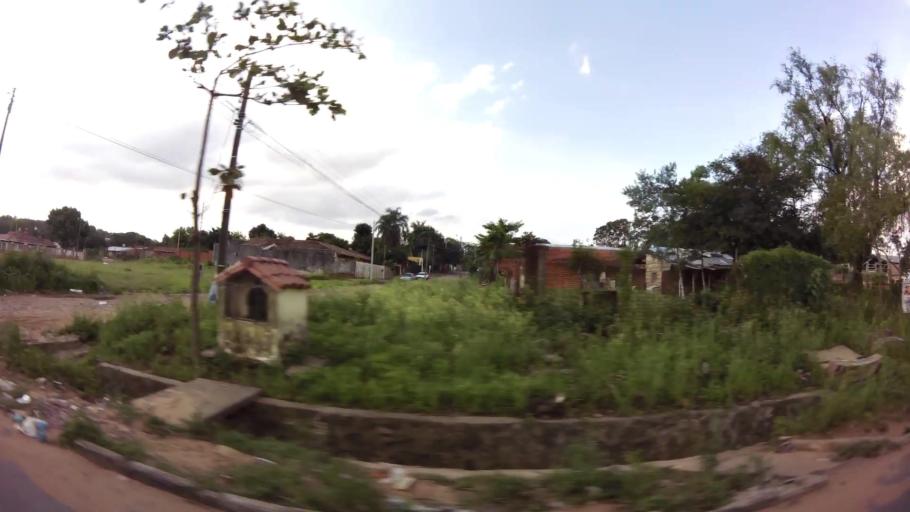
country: PY
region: Central
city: Villa Elisa
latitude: -25.3563
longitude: -57.5577
